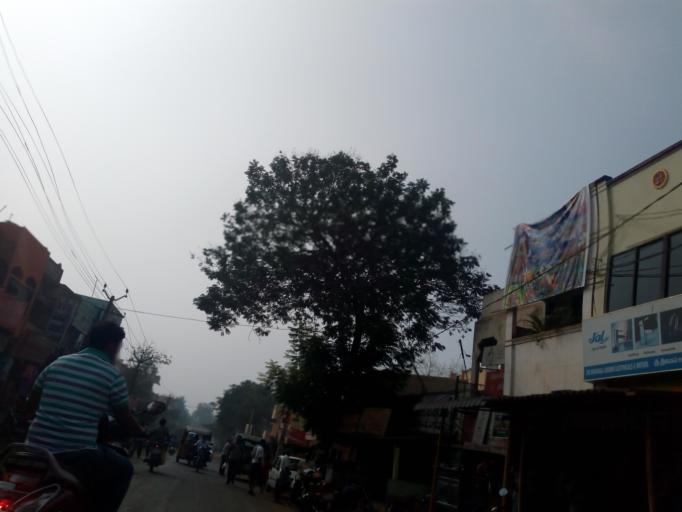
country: IN
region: Andhra Pradesh
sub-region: West Godavari
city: Tadepallegudem
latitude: 16.8197
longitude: 81.4052
